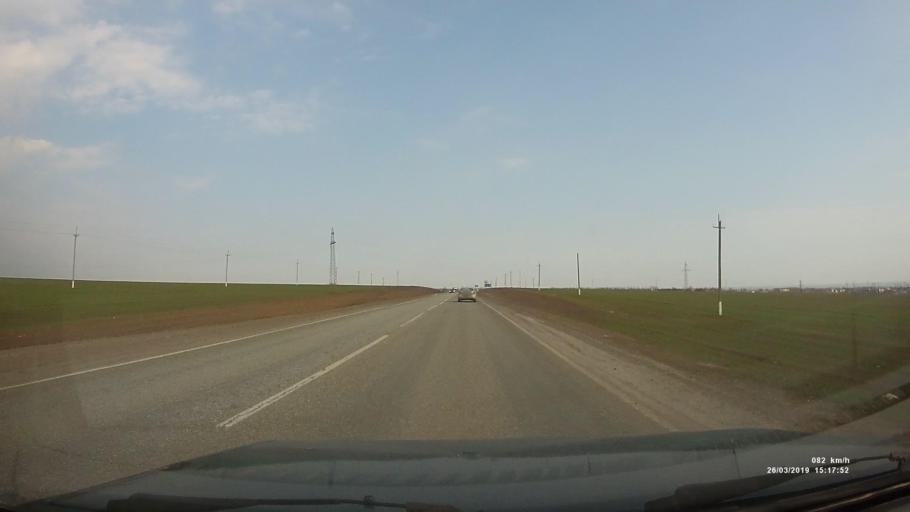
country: RU
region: Rostov
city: Taganrog
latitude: 47.2869
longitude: 38.9280
